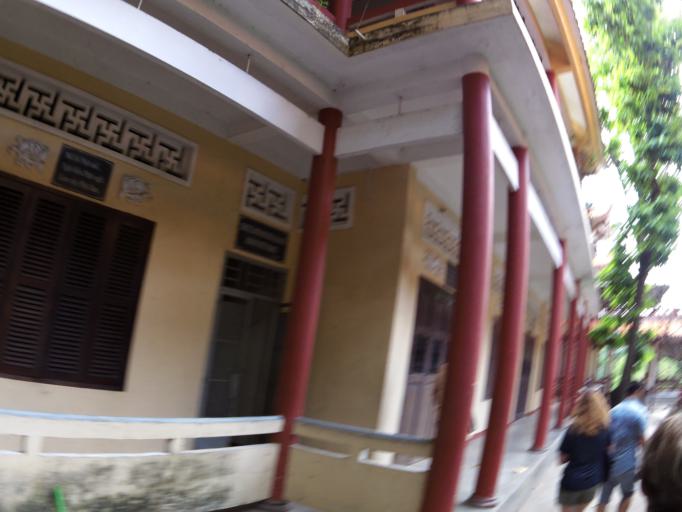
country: VN
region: Khanh Hoa
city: Nha Trang
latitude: 12.2514
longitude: 109.1808
